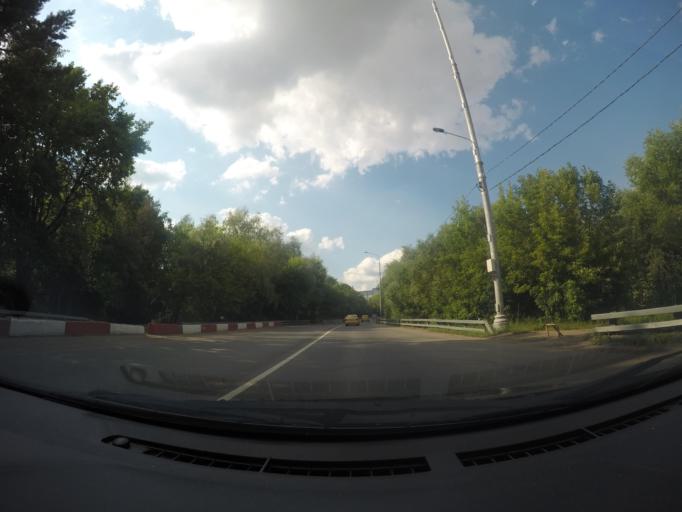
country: RU
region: Moscow
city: Sviblovo
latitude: 55.8432
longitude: 37.6276
